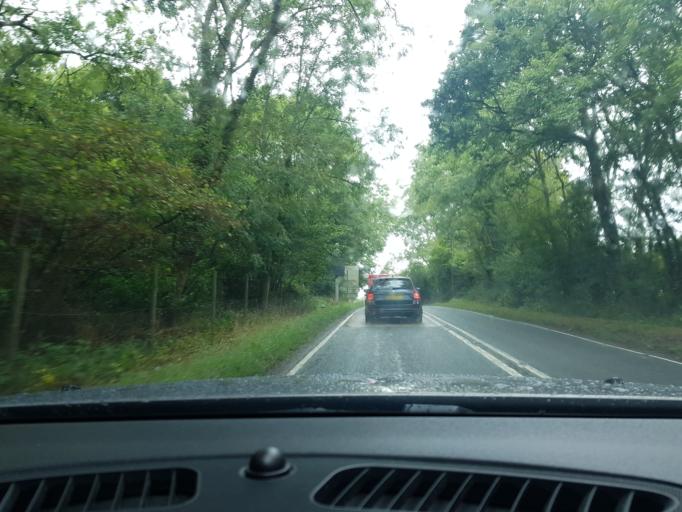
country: GB
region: England
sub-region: Hampshire
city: Fleet
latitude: 51.2457
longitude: -0.8526
